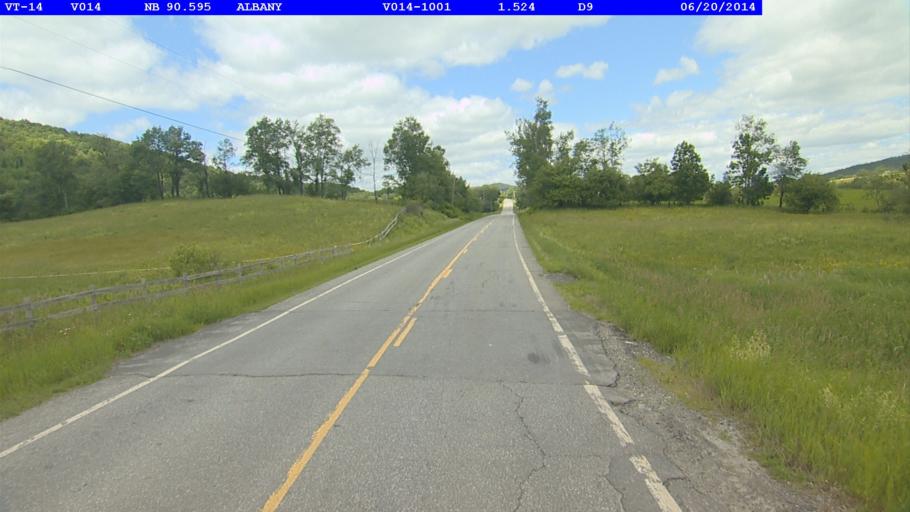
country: US
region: Vermont
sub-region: Caledonia County
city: Hardwick
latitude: 44.7235
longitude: -72.3837
